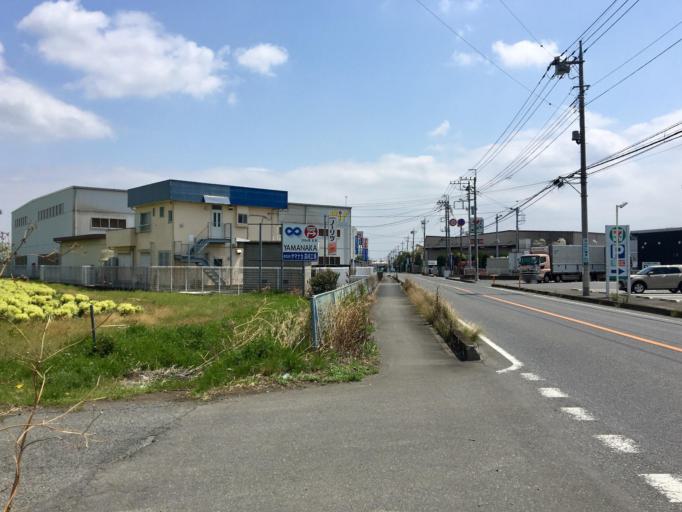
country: JP
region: Gunma
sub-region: Sawa-gun
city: Tamamura
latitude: 36.2963
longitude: 139.1376
